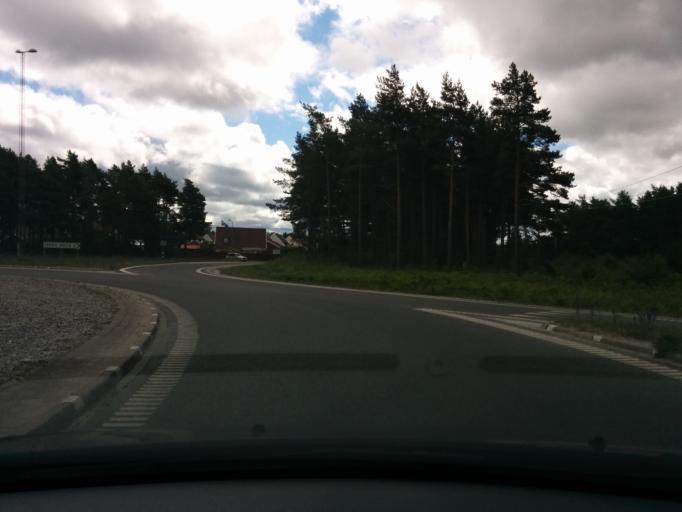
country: SE
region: Gotland
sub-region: Gotland
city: Visby
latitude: 57.6082
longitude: 18.2992
